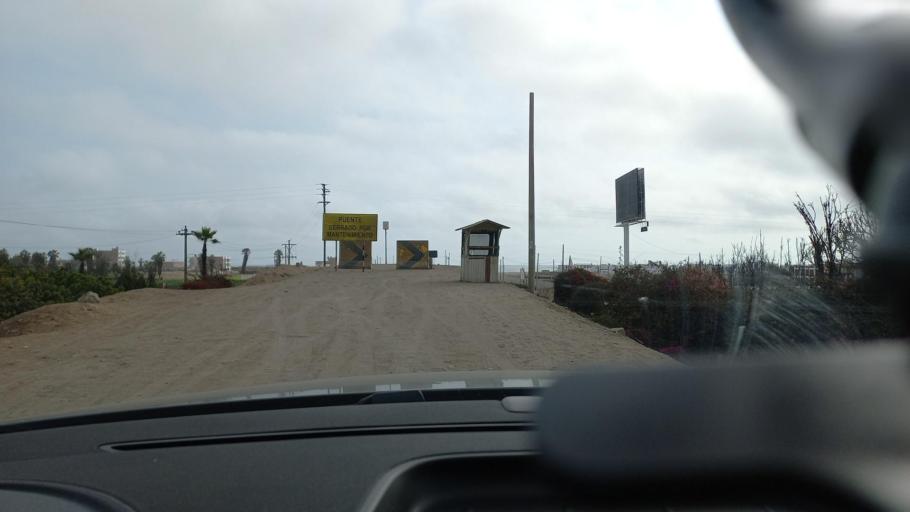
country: PE
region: Lima
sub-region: Lima
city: Punta Hermosa
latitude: -12.2643
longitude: -76.9071
